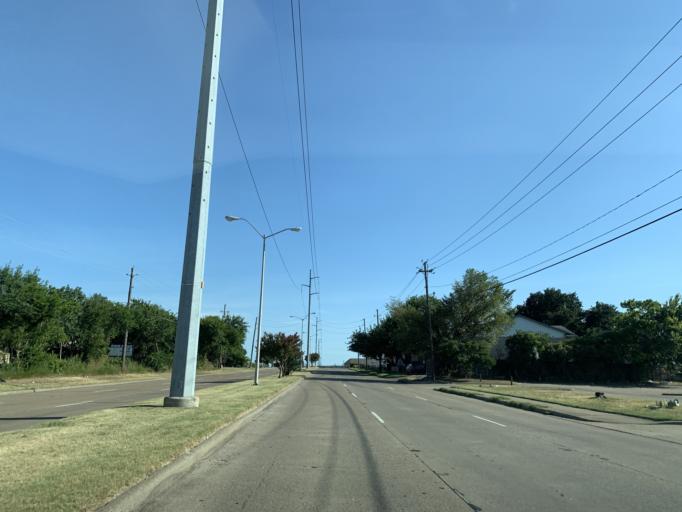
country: US
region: Texas
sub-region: Dallas County
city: Cockrell Hill
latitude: 32.6950
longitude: -96.8915
